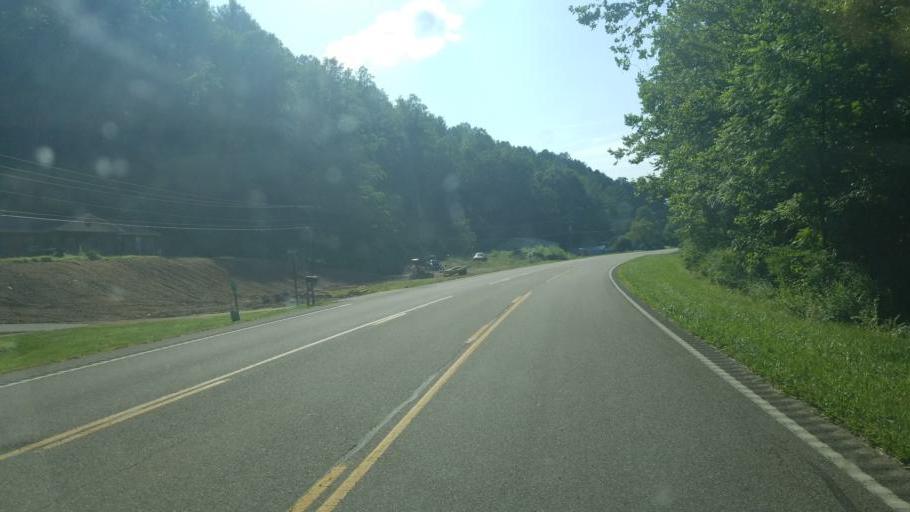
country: US
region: Tennessee
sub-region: Carter County
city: Roan Mountain
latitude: 36.2024
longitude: -82.0782
